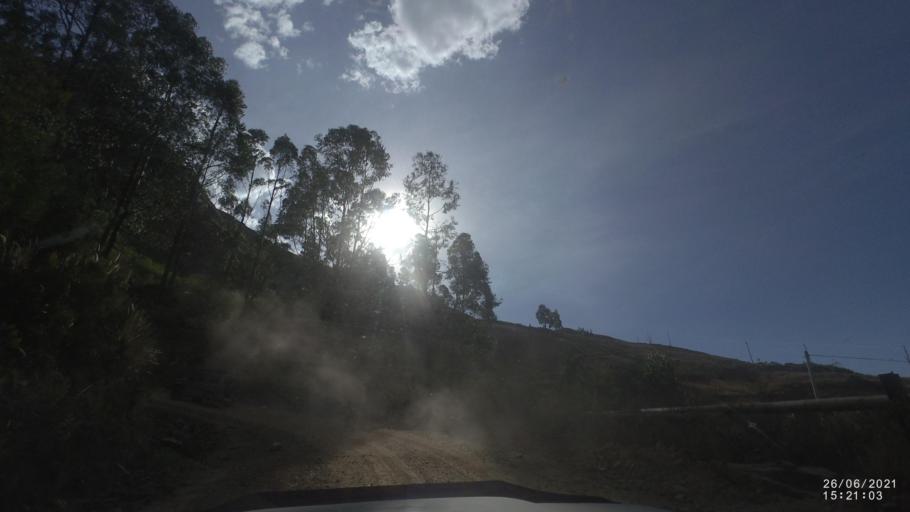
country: BO
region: Cochabamba
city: Mizque
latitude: -17.9410
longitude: -65.6626
